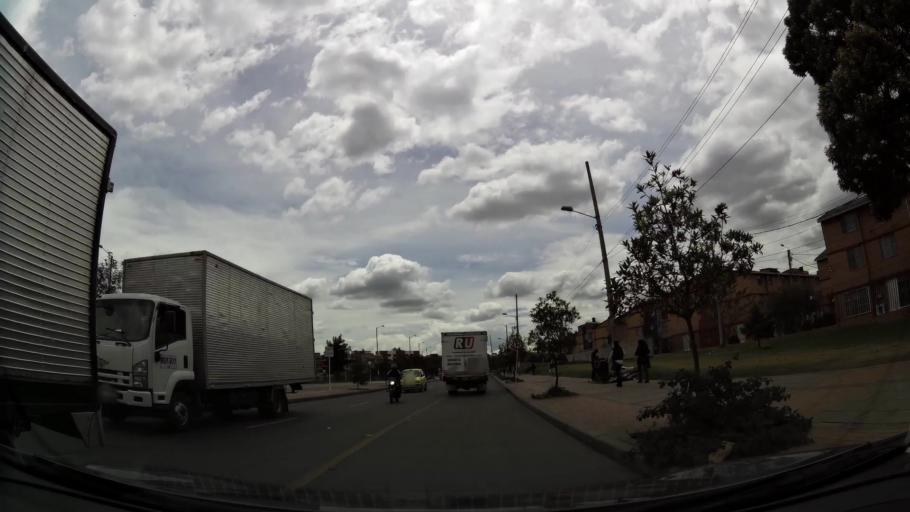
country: CO
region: Cundinamarca
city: Funza
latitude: 4.7115
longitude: -74.1271
